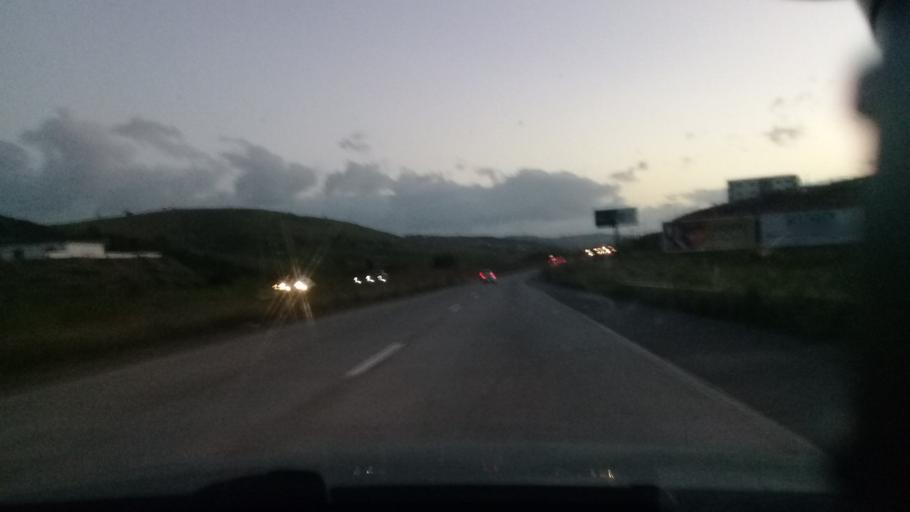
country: BR
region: Pernambuco
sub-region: Vitoria De Santo Antao
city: Vitoria de Santo Antao
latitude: -8.1216
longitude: -35.2677
